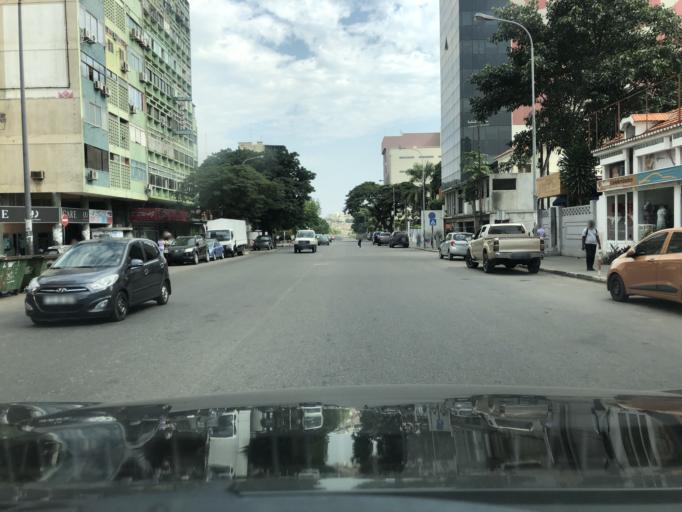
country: AO
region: Luanda
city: Luanda
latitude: -8.8238
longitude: 13.2287
